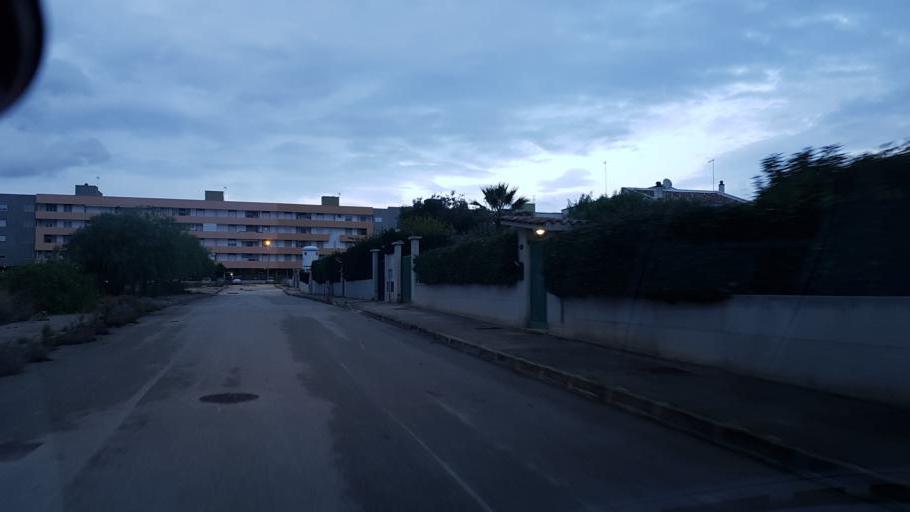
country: IT
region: Apulia
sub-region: Provincia di Taranto
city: Paolo VI
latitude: 40.5301
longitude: 17.2848
